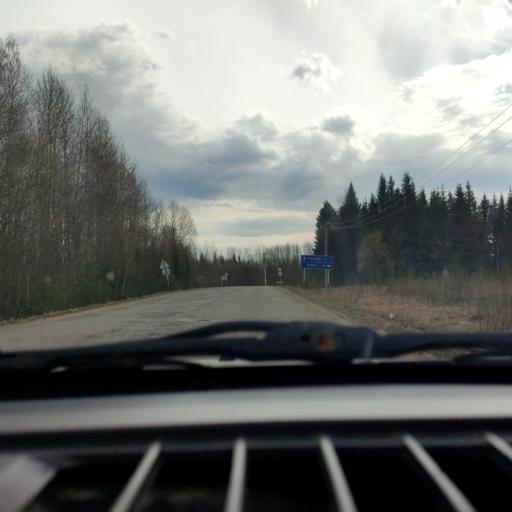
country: RU
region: Perm
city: Polazna
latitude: 58.3400
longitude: 56.1782
